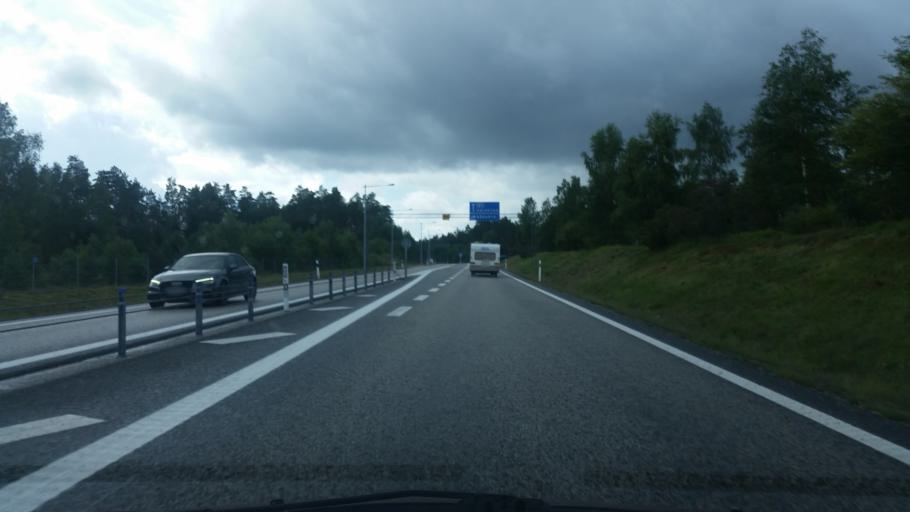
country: SE
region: Joenkoeping
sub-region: Gislaveds Kommun
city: Gislaved
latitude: 57.3430
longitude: 13.5522
